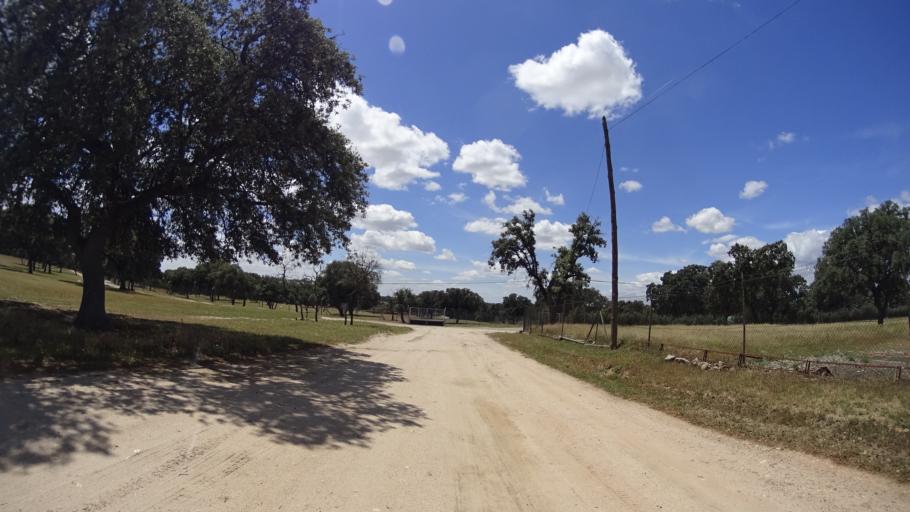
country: ES
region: Madrid
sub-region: Provincia de Madrid
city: Brunete
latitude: 40.4292
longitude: -3.9670
